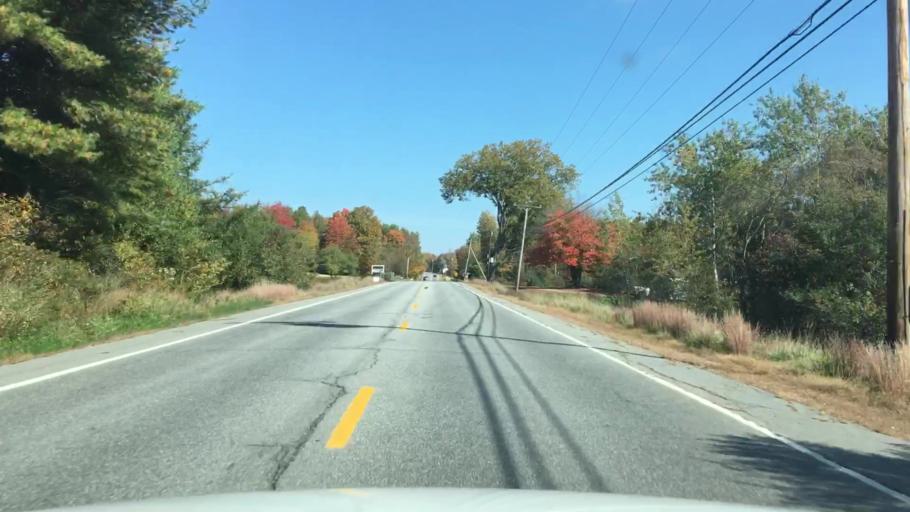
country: US
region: Maine
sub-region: Sagadahoc County
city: Topsham
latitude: 43.9844
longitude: -69.9581
